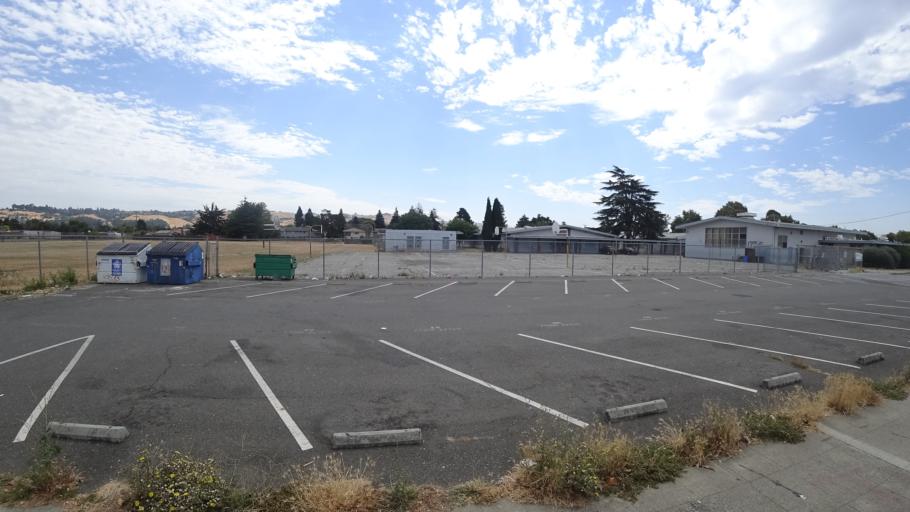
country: US
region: California
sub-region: Alameda County
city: Hayward
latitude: 37.6419
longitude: -122.0812
